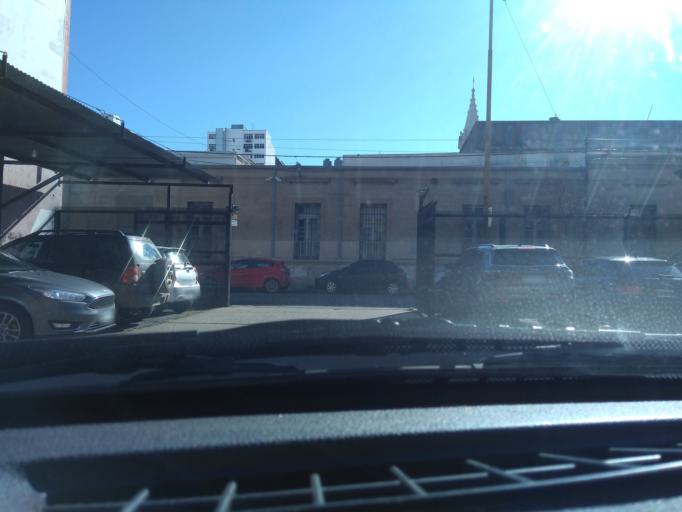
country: AR
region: Santa Fe
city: Santa Fe de la Vera Cruz
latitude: -31.6513
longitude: -60.7097
